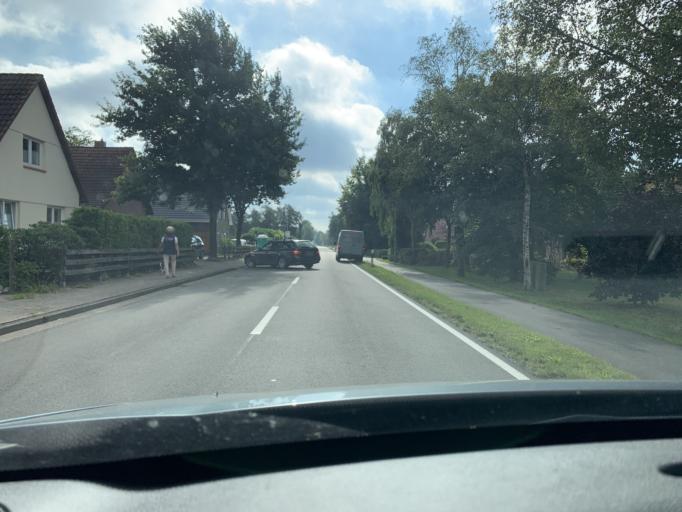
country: DE
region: Lower Saxony
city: Edewecht
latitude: 53.1002
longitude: 8.0806
